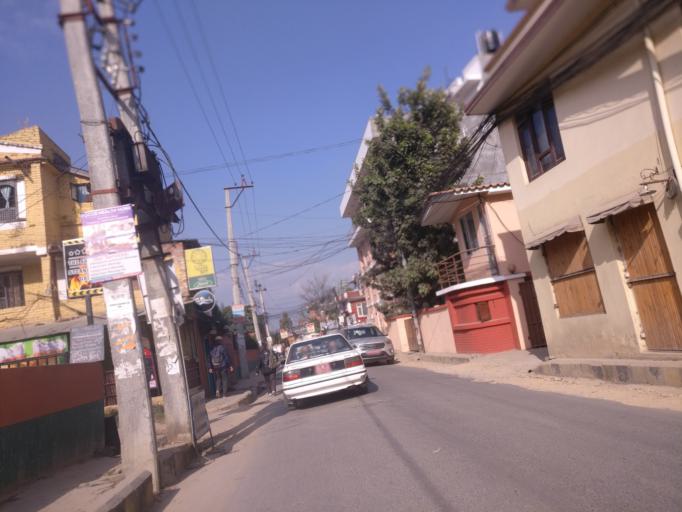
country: NP
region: Central Region
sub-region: Bagmati Zone
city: Patan
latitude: 27.6849
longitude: 85.3126
